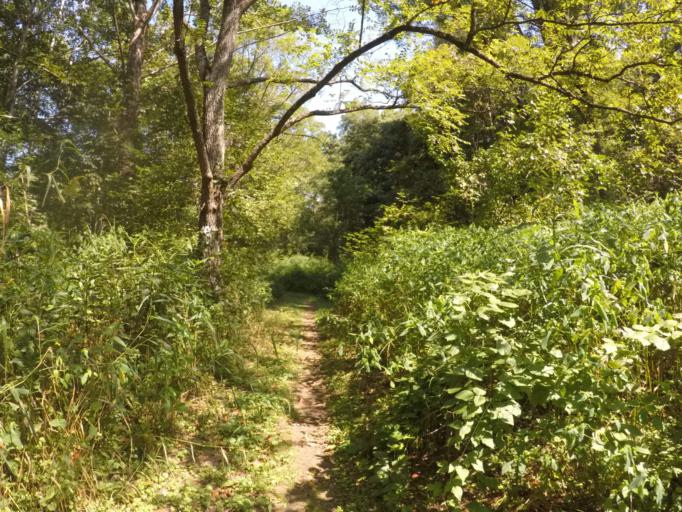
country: US
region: Ohio
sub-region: Lawrence County
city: Ironton
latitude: 38.6309
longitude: -82.6074
